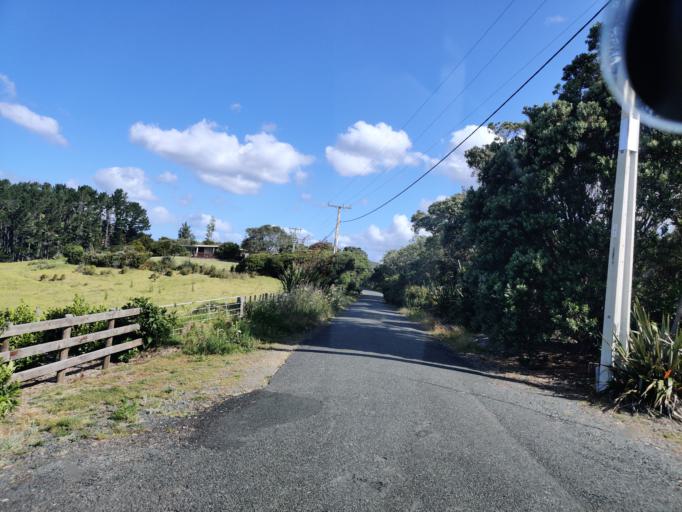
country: NZ
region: Northland
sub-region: Whangarei
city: Ngunguru
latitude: -35.6086
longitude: 174.5292
